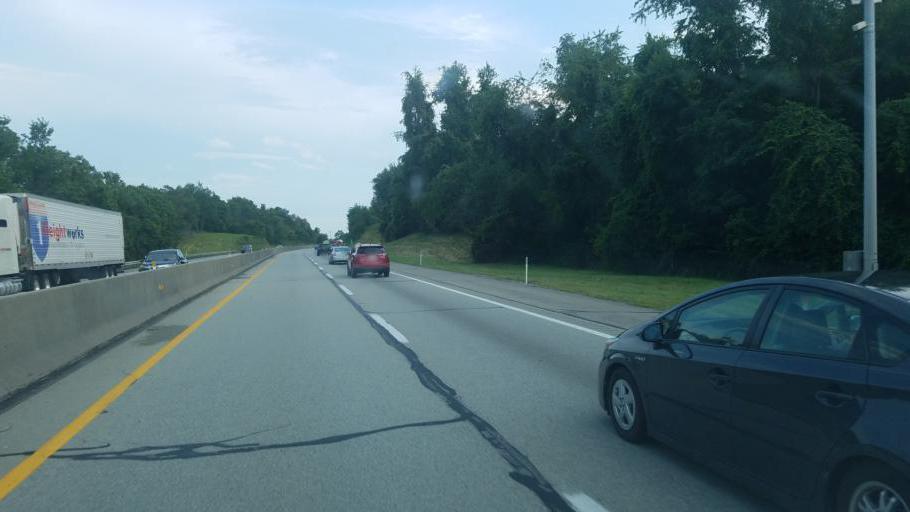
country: US
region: Pennsylvania
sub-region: Allegheny County
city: Plum
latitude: 40.4559
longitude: -79.7564
